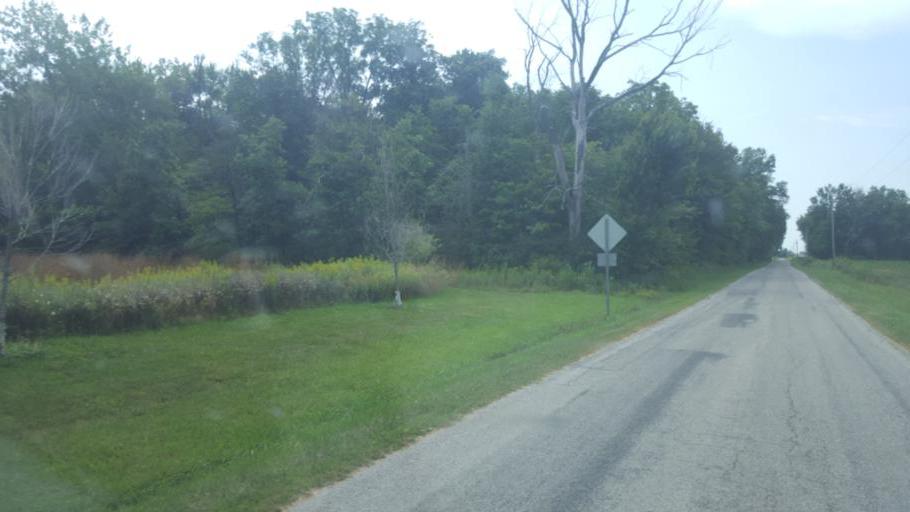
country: US
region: Ohio
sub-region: Delaware County
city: Ashley
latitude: 40.4942
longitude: -83.0246
